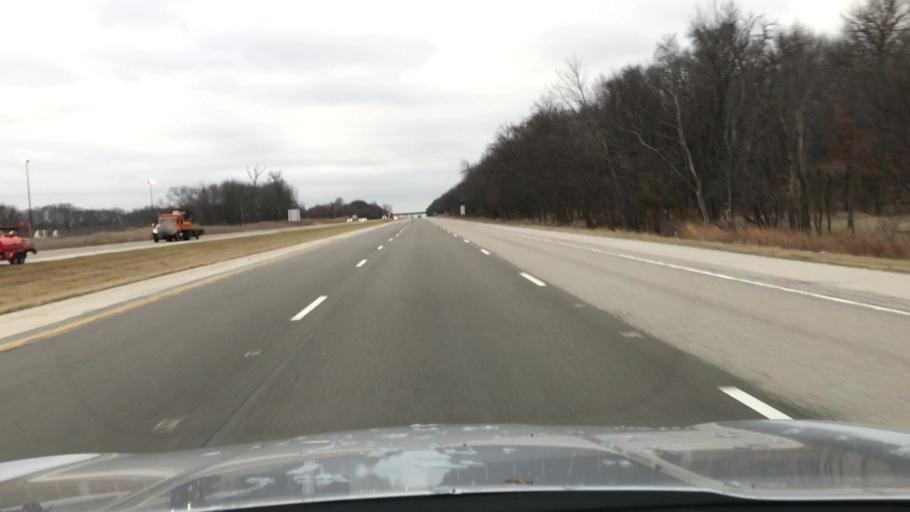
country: US
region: Illinois
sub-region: Logan County
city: Lincoln
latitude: 40.1565
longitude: -89.4177
